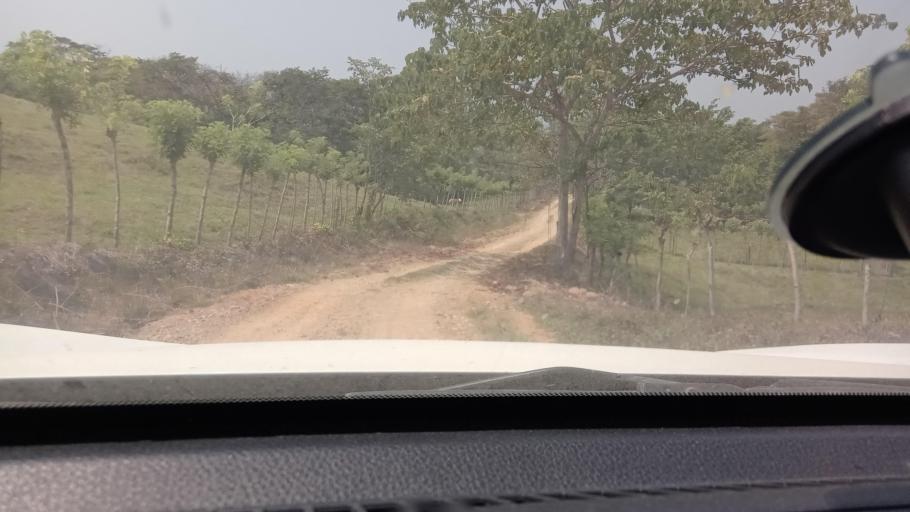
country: MX
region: Tabasco
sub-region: Huimanguillo
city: Francisco Rueda
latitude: 17.4910
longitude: -93.9307
